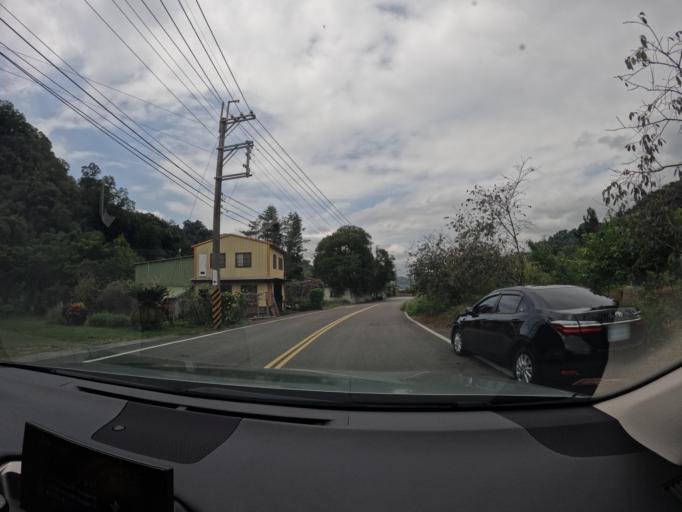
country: TW
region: Taiwan
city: Fengyuan
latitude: 24.3309
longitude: 120.8763
